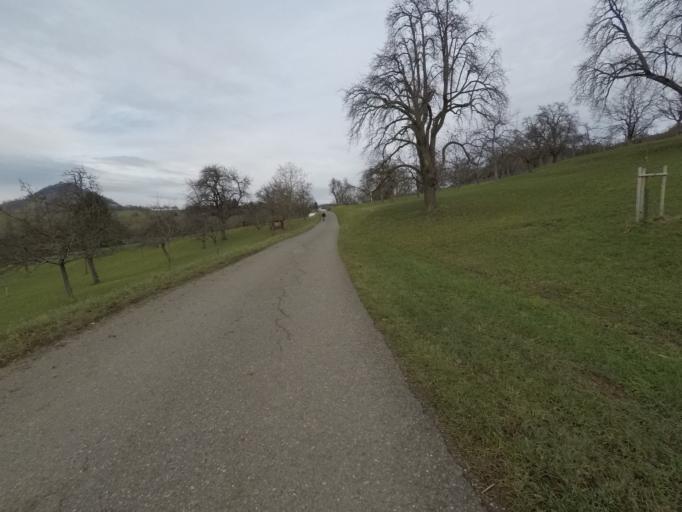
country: DE
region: Baden-Wuerttemberg
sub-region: Tuebingen Region
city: Eningen unter Achalm
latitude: 48.4767
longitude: 9.2639
